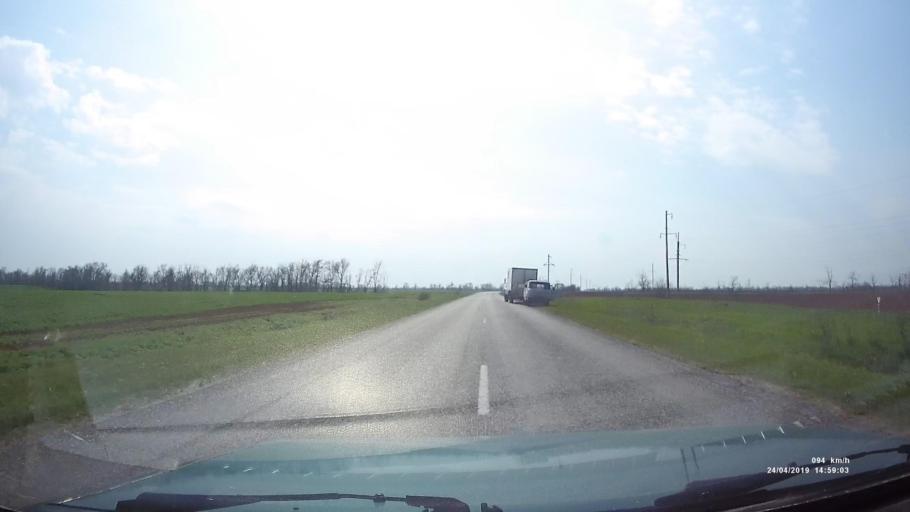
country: RU
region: Rostov
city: Remontnoye
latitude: 46.5671
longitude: 43.5823
